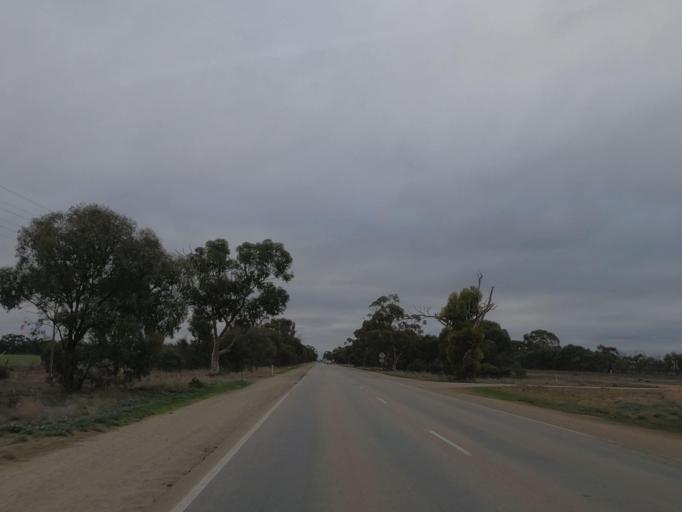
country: AU
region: Victoria
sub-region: Swan Hill
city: Swan Hill
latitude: -35.4049
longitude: 143.5805
